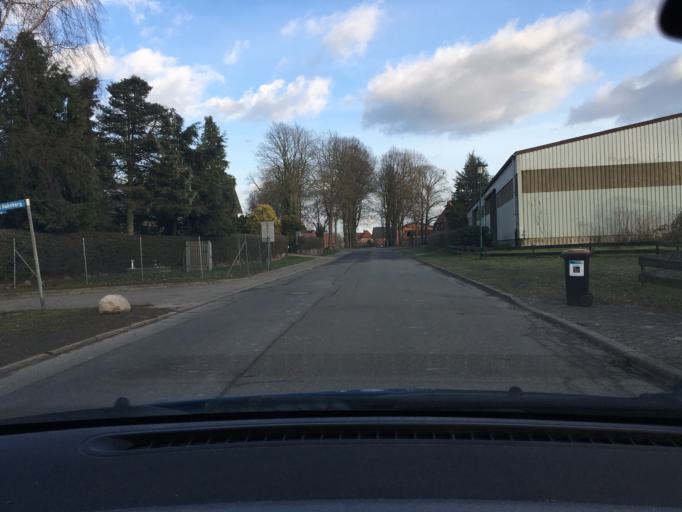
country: DE
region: Schleswig-Holstein
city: Wangelau
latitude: 53.4536
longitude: 10.5434
